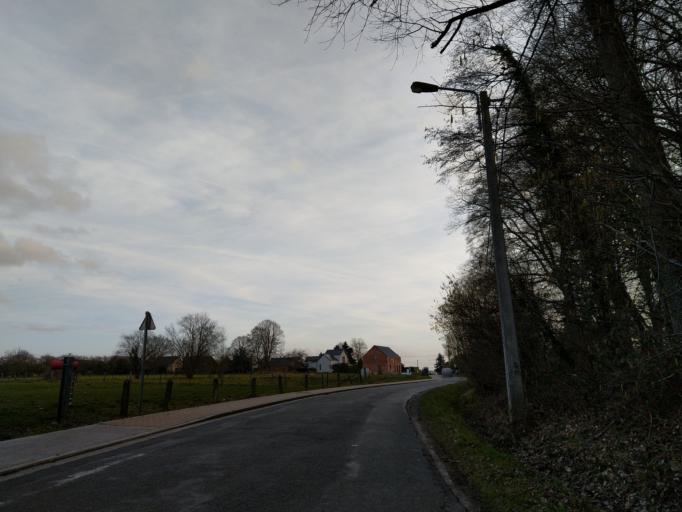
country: BE
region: Wallonia
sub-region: Province du Hainaut
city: Jurbise
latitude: 50.5159
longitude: 3.9505
